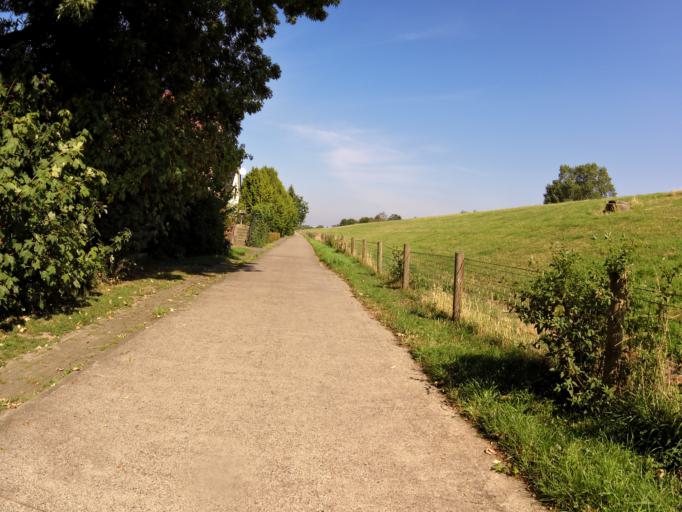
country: DE
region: Lower Saxony
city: Elsfleth
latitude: 53.2713
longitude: 8.4805
